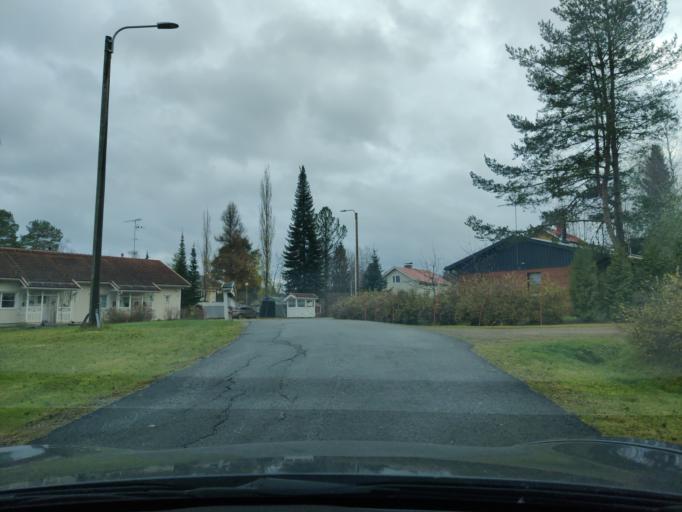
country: FI
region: Northern Savo
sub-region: Ylae-Savo
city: Kiuruvesi
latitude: 63.6508
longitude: 26.6345
